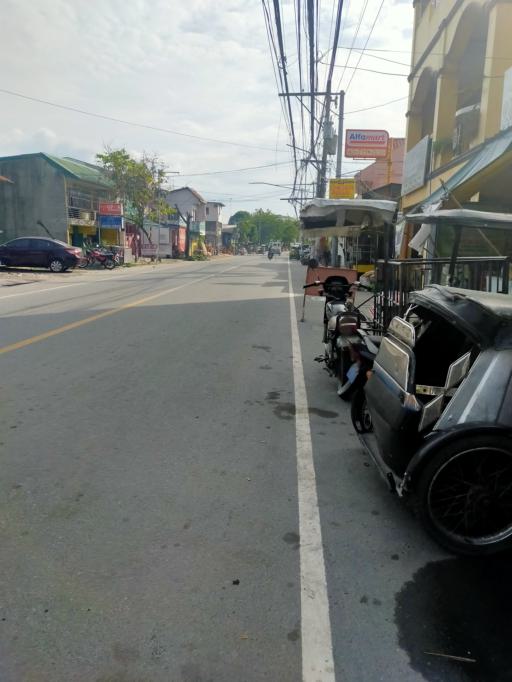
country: PH
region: Central Luzon
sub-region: Province of Pampanga
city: Pau
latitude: 15.0080
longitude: 120.7103
